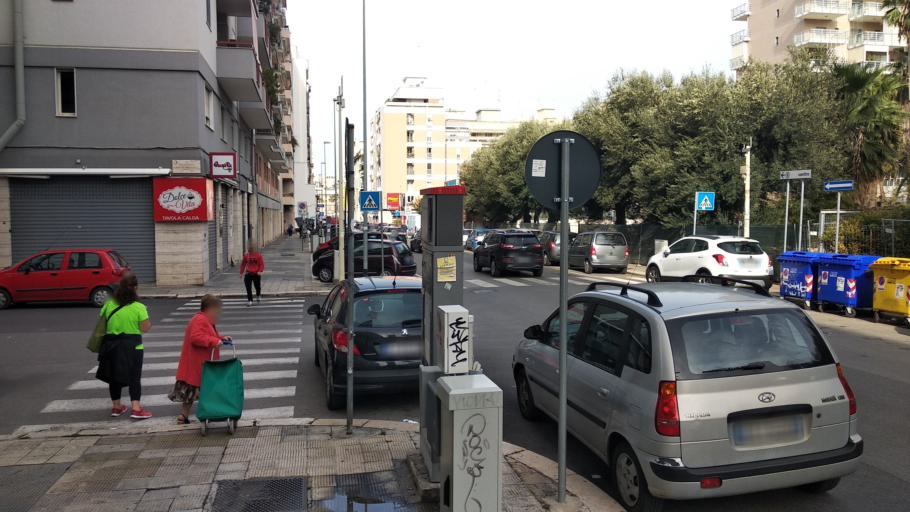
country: IT
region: Apulia
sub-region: Provincia di Bari
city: Bari
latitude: 41.1155
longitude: 16.8797
